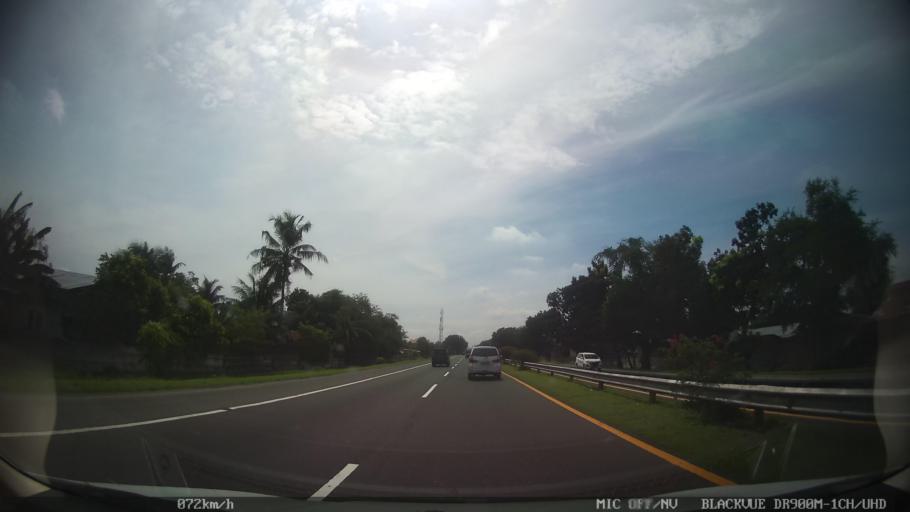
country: ID
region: North Sumatra
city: Medan
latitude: 3.6440
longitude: 98.6911
